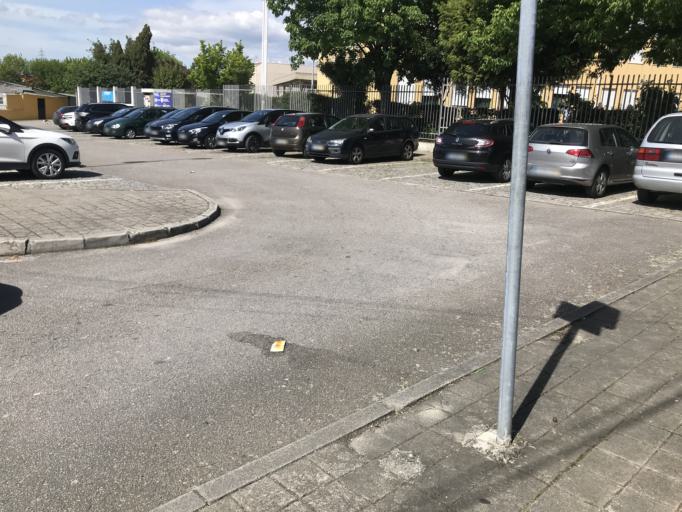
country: PT
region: Porto
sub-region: Matosinhos
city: Matosinhos
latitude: 41.1828
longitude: -8.6714
